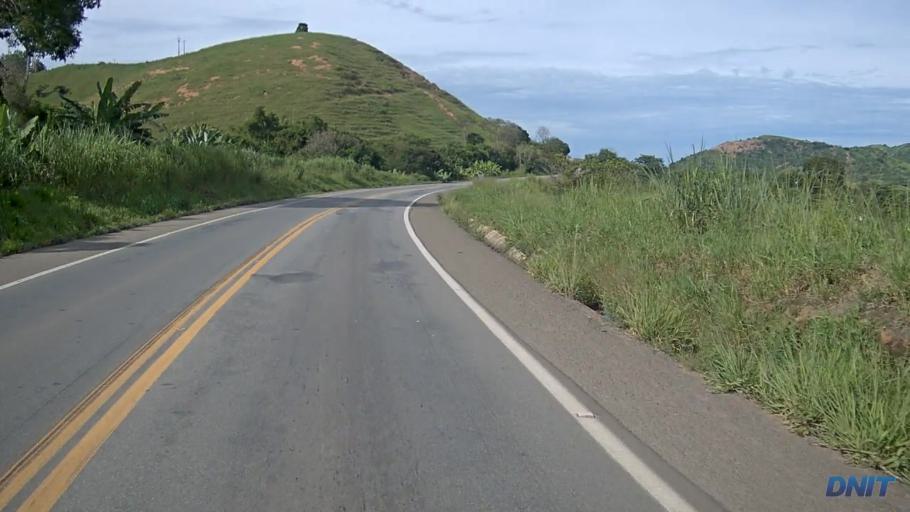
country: BR
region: Minas Gerais
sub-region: Belo Oriente
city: Belo Oriente
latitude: -19.1662
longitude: -42.2452
